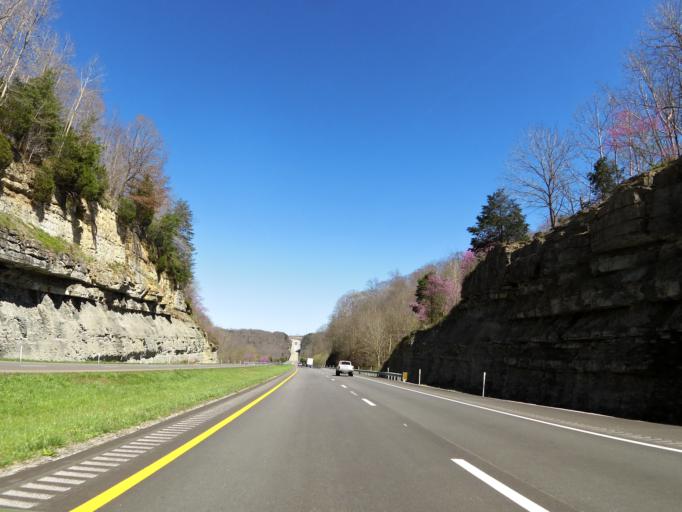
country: US
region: Kentucky
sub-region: Pulaski County
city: Somerset
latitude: 37.0959
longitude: -84.7059
